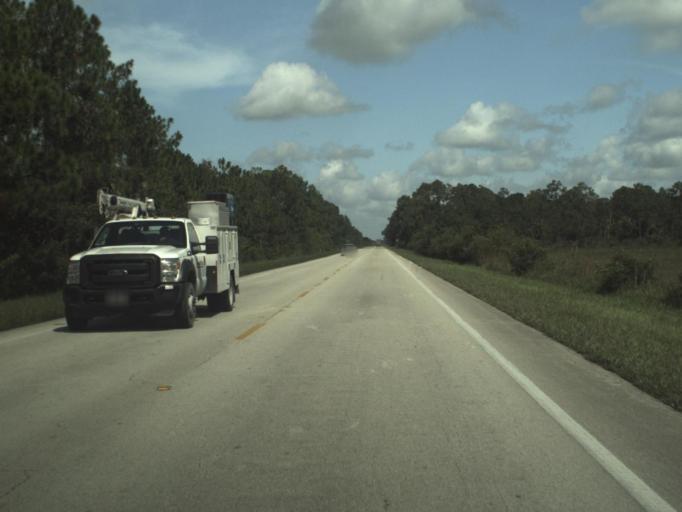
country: US
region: Florida
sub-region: Martin County
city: Indiantown
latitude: 26.9776
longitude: -80.4033
